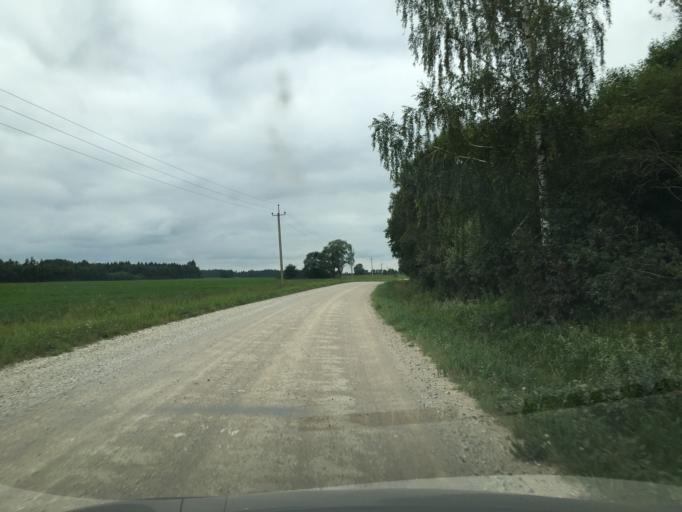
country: EE
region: Raplamaa
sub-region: Jaervakandi vald
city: Jarvakandi
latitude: 58.7942
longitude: 24.9523
